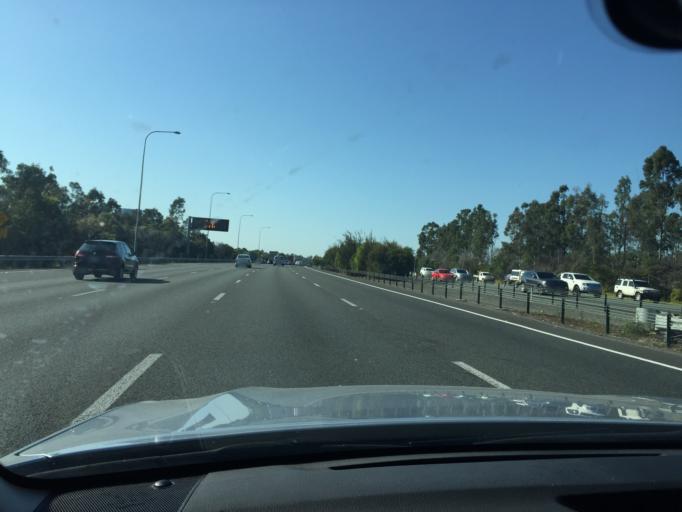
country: AU
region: Queensland
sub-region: Gold Coast
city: Yatala
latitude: -27.7226
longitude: 153.2173
